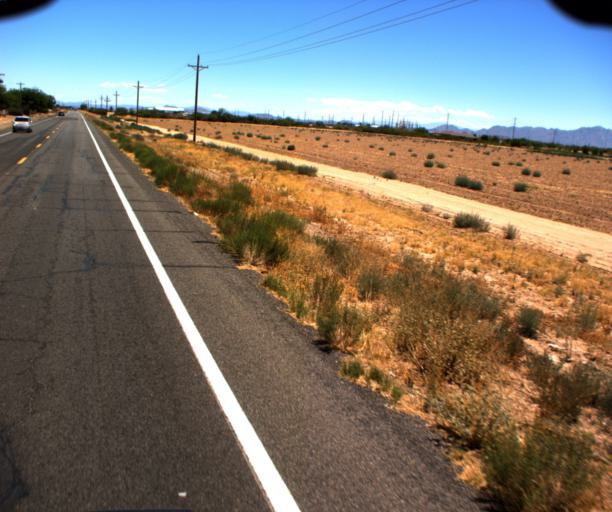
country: US
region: Arizona
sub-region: Pinal County
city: Coolidge
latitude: 32.8796
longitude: -111.5801
